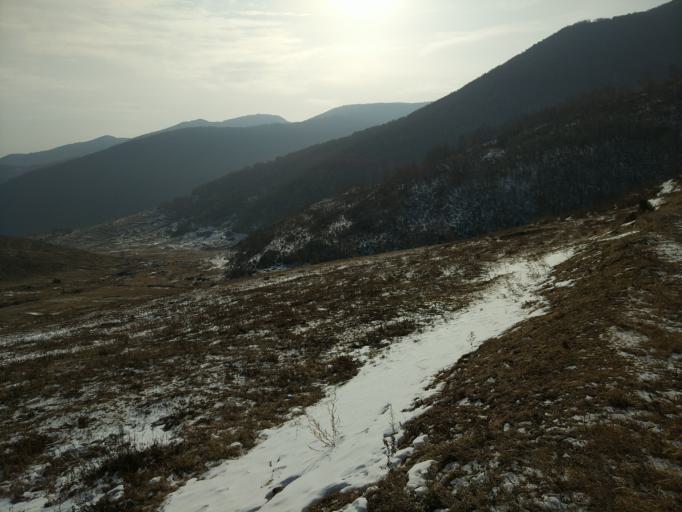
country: CN
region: Hebei
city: Xiwanzi
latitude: 40.8575
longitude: 115.4554
